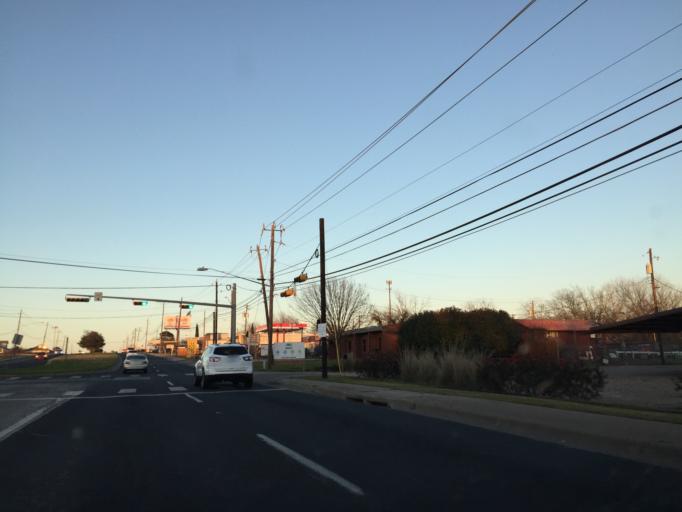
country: US
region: Texas
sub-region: Travis County
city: Pflugerville
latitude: 30.3967
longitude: -97.6429
